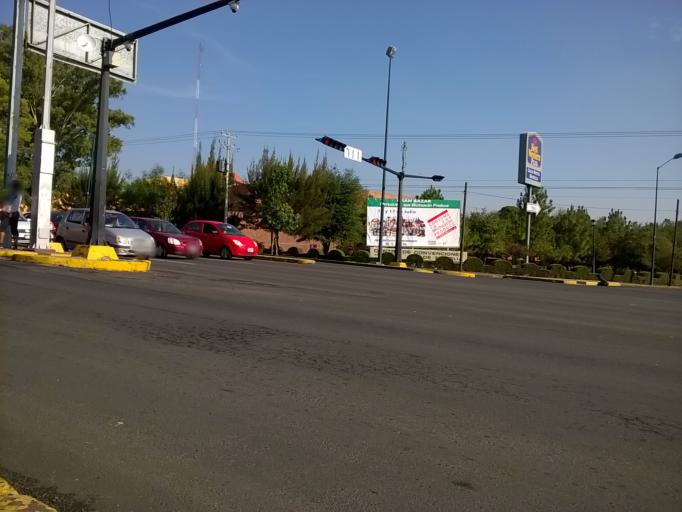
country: MX
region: Michoacan
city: Morelia
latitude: 19.6811
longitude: -101.1814
